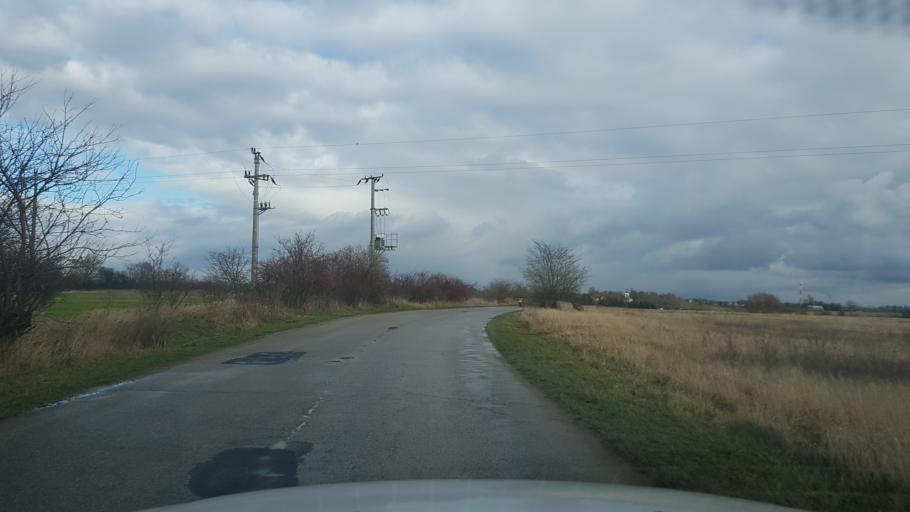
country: PL
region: West Pomeranian Voivodeship
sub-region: Powiat policki
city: Przeclaw
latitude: 53.4111
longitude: 14.4138
